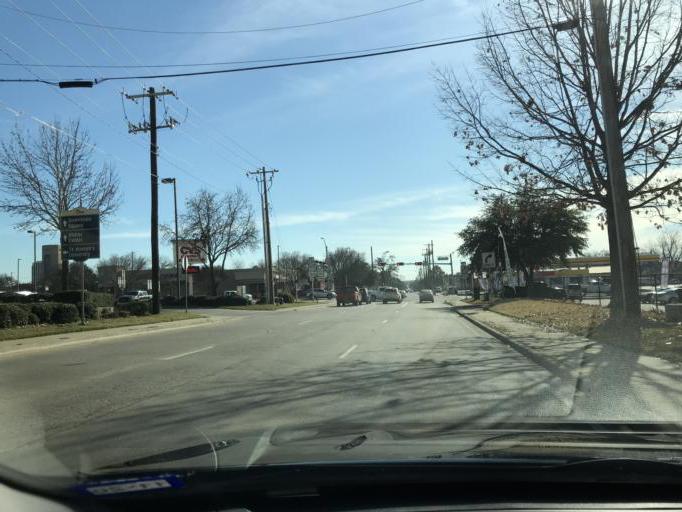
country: US
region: Texas
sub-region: Denton County
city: Denton
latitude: 33.2317
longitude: -97.1335
